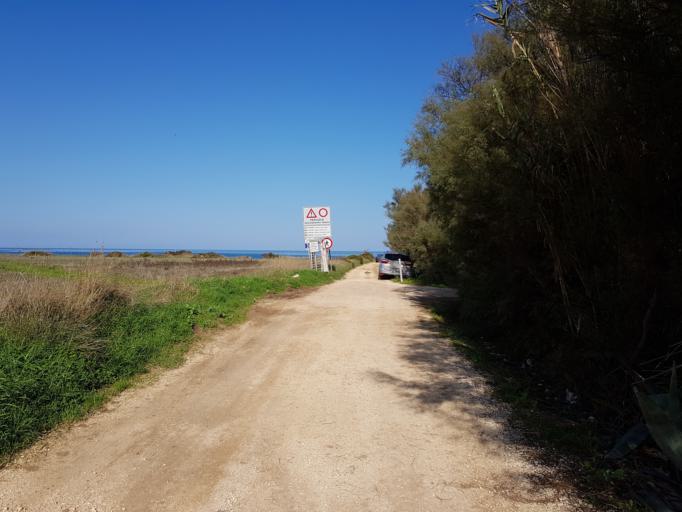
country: IT
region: Apulia
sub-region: Provincia di Brindisi
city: San Vito dei Normanni
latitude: 40.6981
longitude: 17.8201
